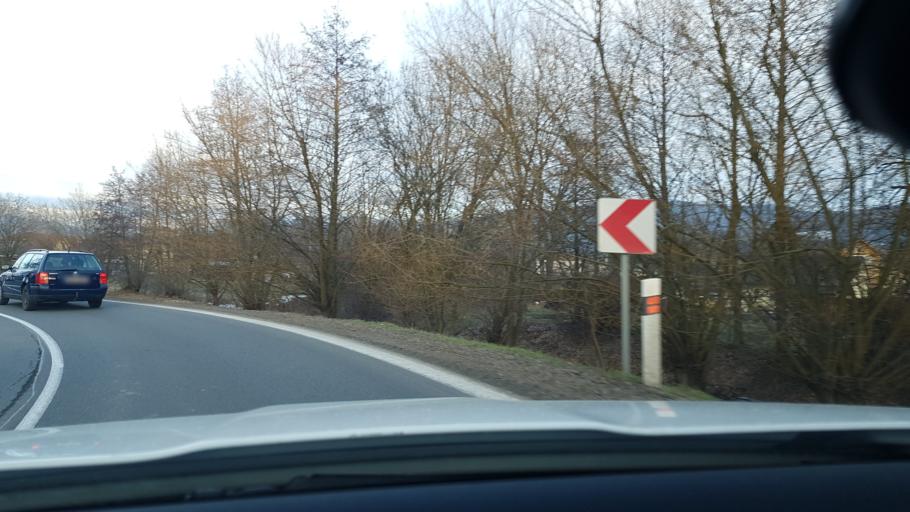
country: CZ
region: Olomoucky
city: Rapotin
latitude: 50.0025
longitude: 17.0209
